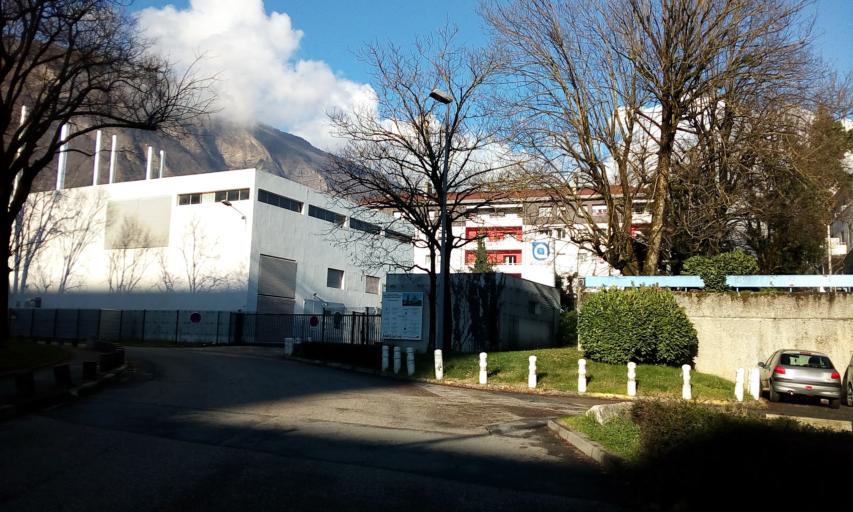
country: FR
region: Rhone-Alpes
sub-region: Departement de l'Isere
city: La Tronche
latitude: 45.2003
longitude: 5.7471
